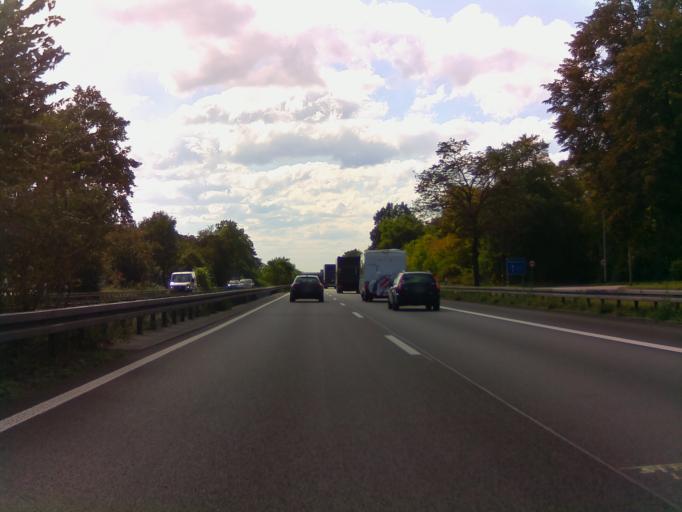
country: DE
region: Hesse
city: Pfungstadt
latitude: 49.8123
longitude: 8.5781
